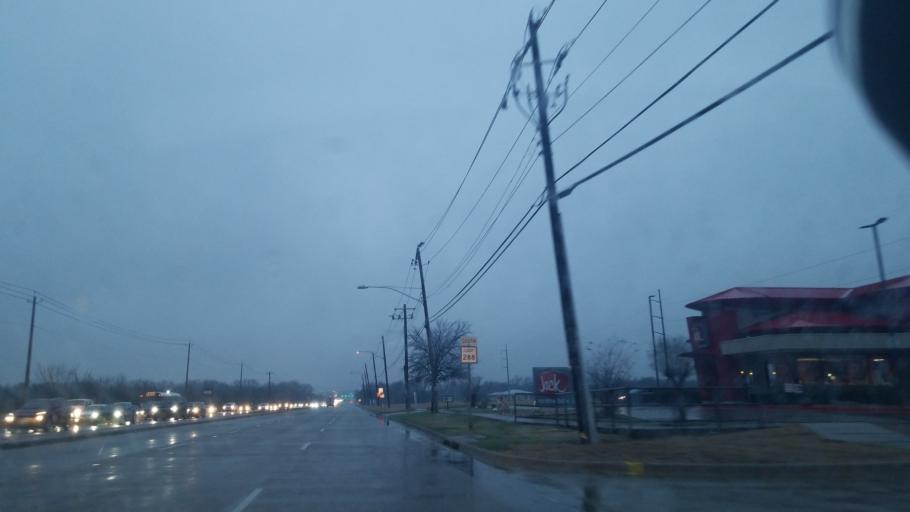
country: US
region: Texas
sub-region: Denton County
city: Denton
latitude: 33.2124
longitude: -97.0908
